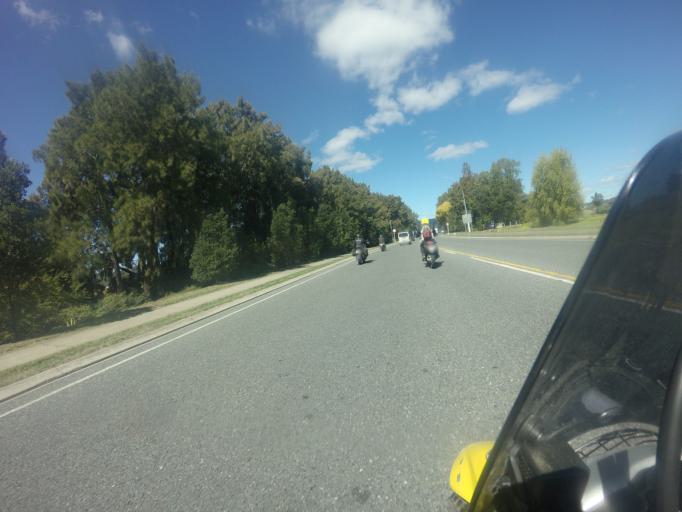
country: NZ
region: Bay of Plenty
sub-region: Whakatane District
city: Whakatane
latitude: -37.9547
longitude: 176.9711
